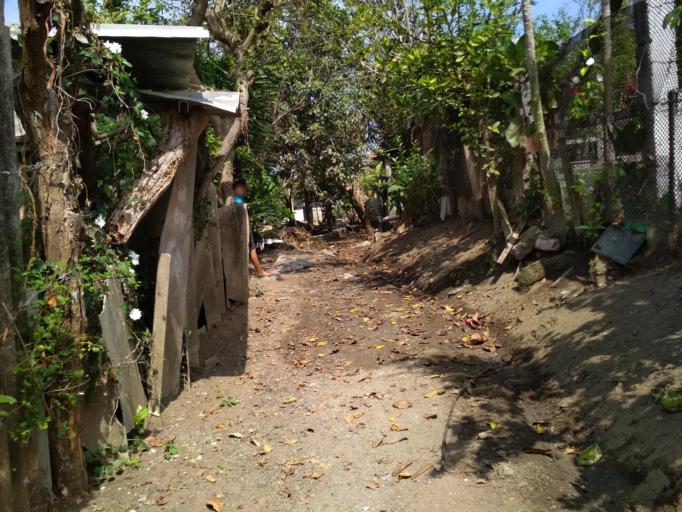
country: MX
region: Veracruz
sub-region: Veracruz
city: Delfino Victoria (Santa Fe)
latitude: 19.2539
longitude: -96.2647
